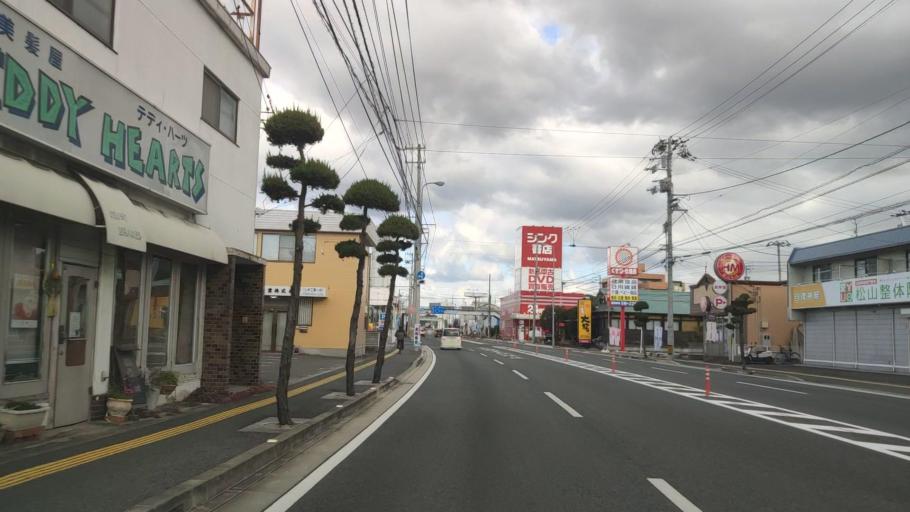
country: JP
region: Ehime
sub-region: Shikoku-chuo Shi
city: Matsuyama
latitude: 33.8703
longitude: 132.7522
